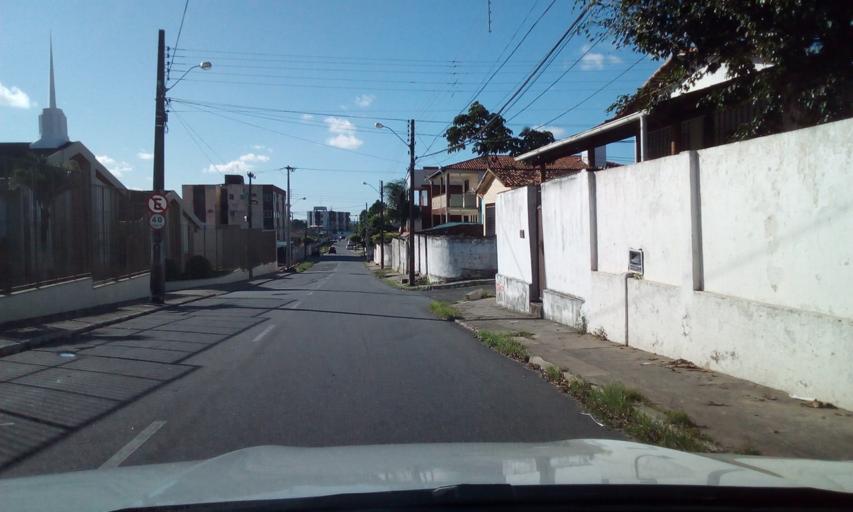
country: BR
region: Paraiba
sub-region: Joao Pessoa
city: Joao Pessoa
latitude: -7.1033
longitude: -34.8589
